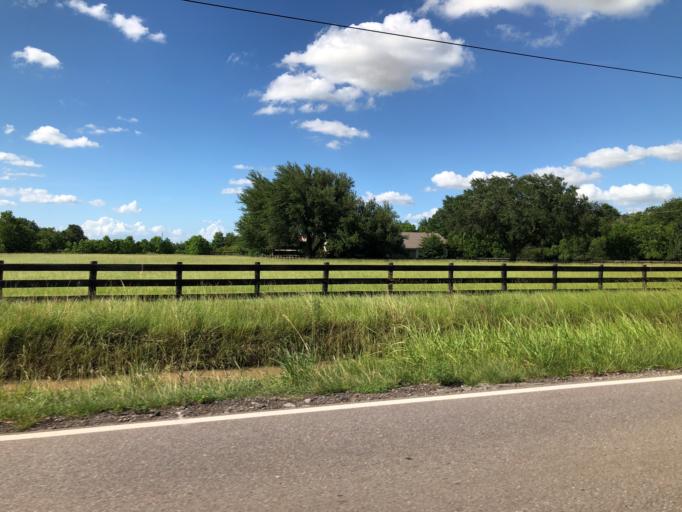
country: US
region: Texas
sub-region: Harris County
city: Katy
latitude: 29.8314
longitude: -95.8015
